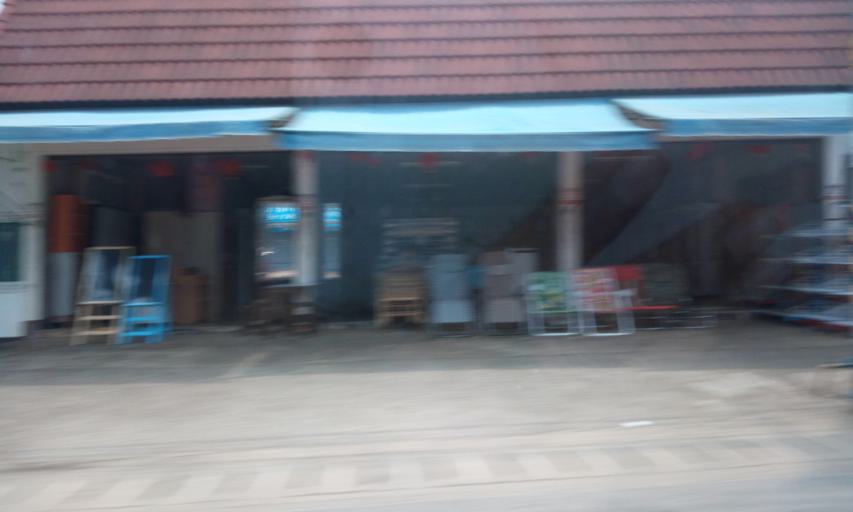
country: TH
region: Phayao
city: Chiang Kham
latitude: 19.5228
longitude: 100.3062
